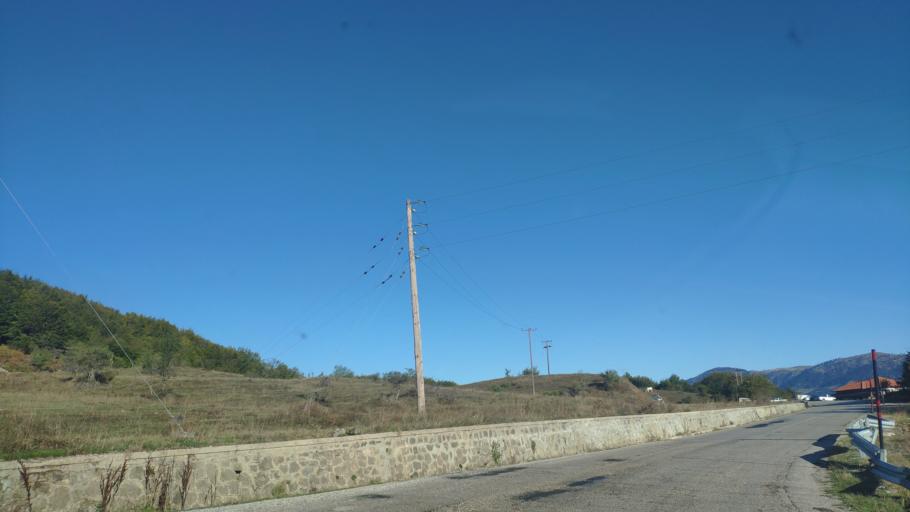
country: GR
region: Epirus
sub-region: Nomos Ioanninon
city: Metsovo
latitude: 39.7792
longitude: 21.1629
